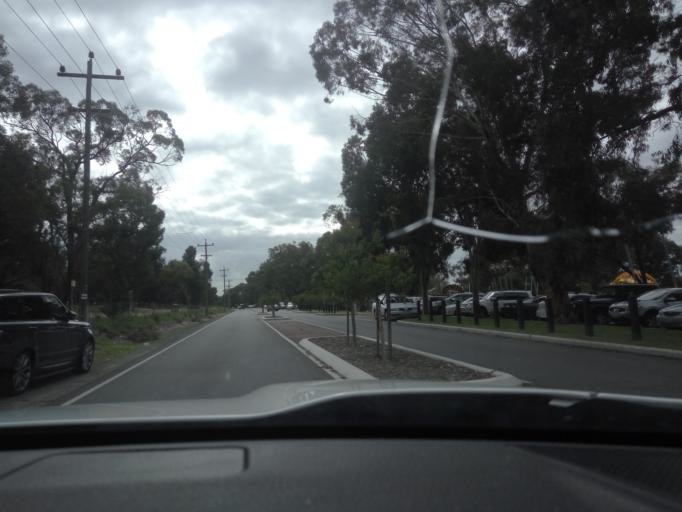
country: AU
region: Western Australia
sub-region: City of Cockburn
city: Bibra Lake
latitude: -32.0884
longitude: 115.8214
